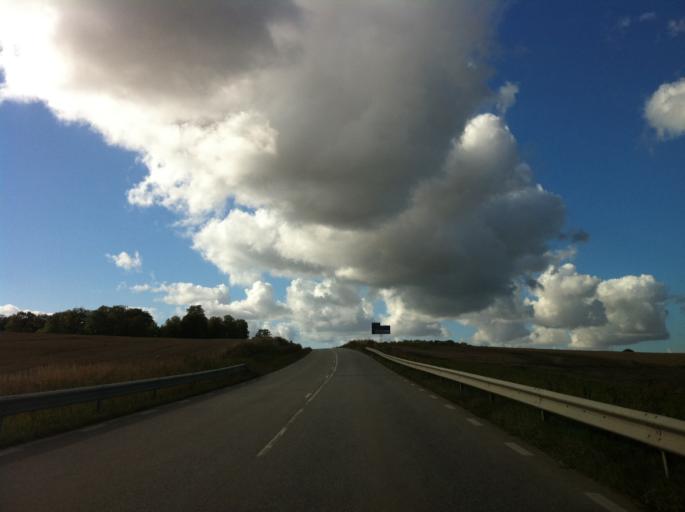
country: SE
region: Skane
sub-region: Eslovs Kommun
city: Eslov
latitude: 55.7873
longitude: 13.2510
